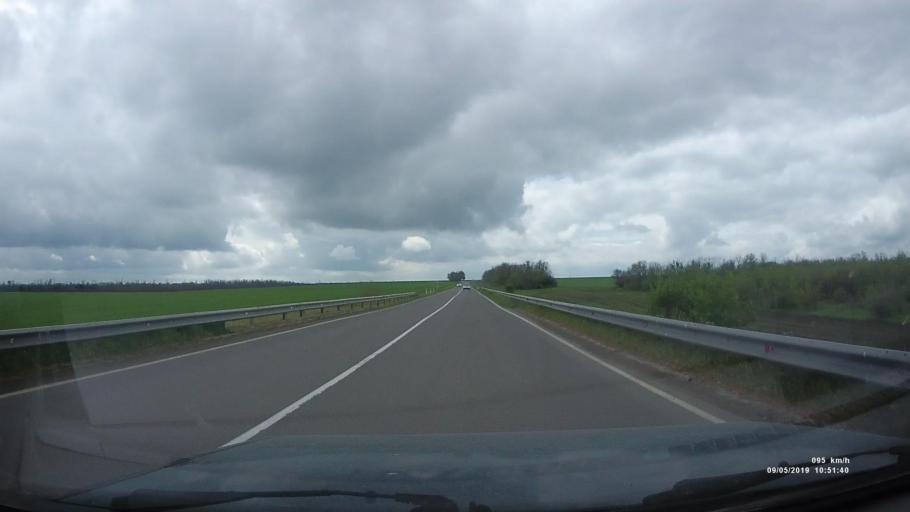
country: RU
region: Rostov
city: Peshkovo
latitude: 46.9117
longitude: 39.3551
